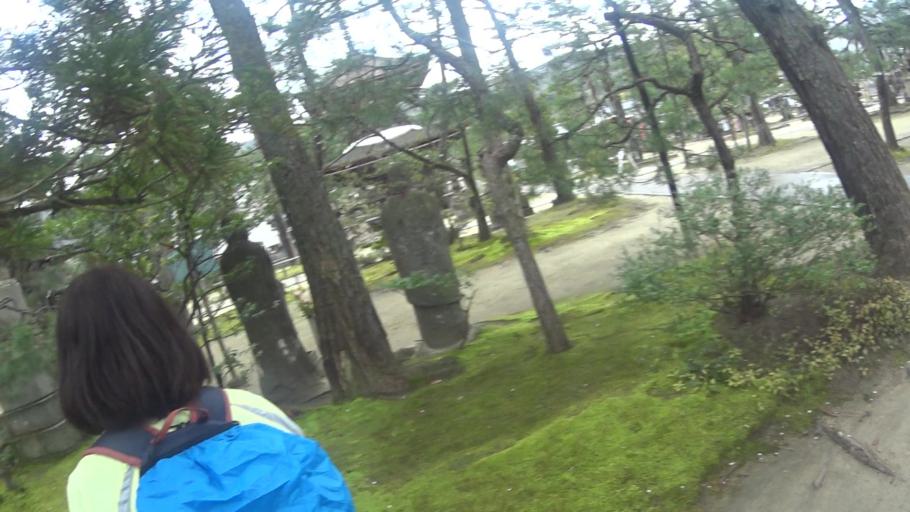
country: JP
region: Kyoto
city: Miyazu
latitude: 35.5582
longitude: 135.1846
